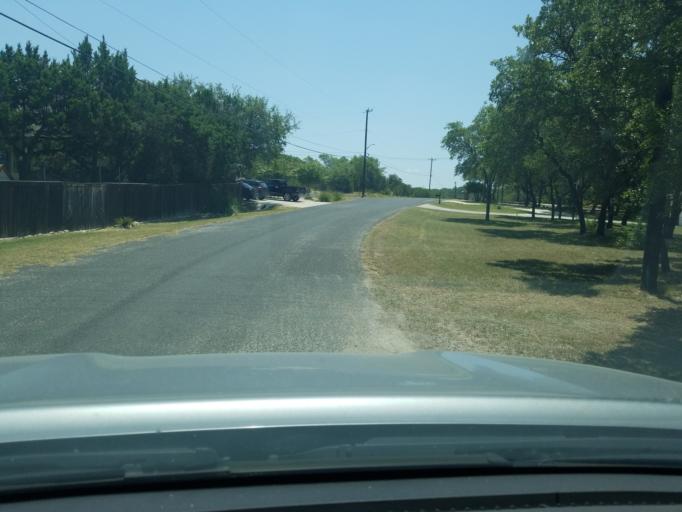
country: US
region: Texas
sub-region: Bexar County
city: Timberwood Park
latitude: 29.6993
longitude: -98.4848
